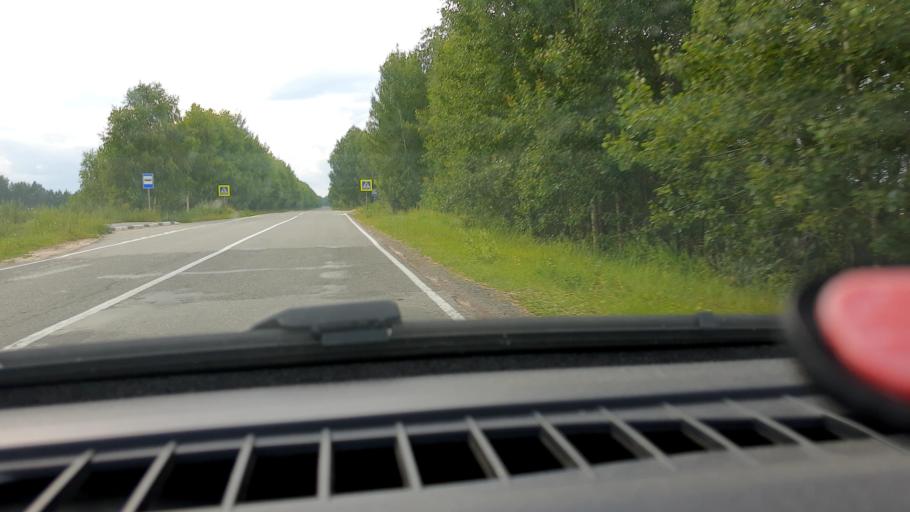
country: RU
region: Nizjnij Novgorod
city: Neklyudovo
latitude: 56.5129
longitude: 43.9443
